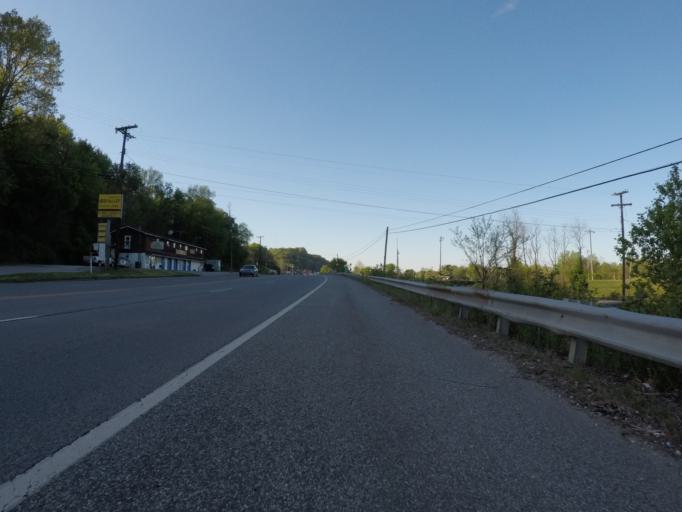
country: US
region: Kentucky
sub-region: Boyd County
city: Catlettsburg
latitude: 38.3976
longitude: -82.6008
